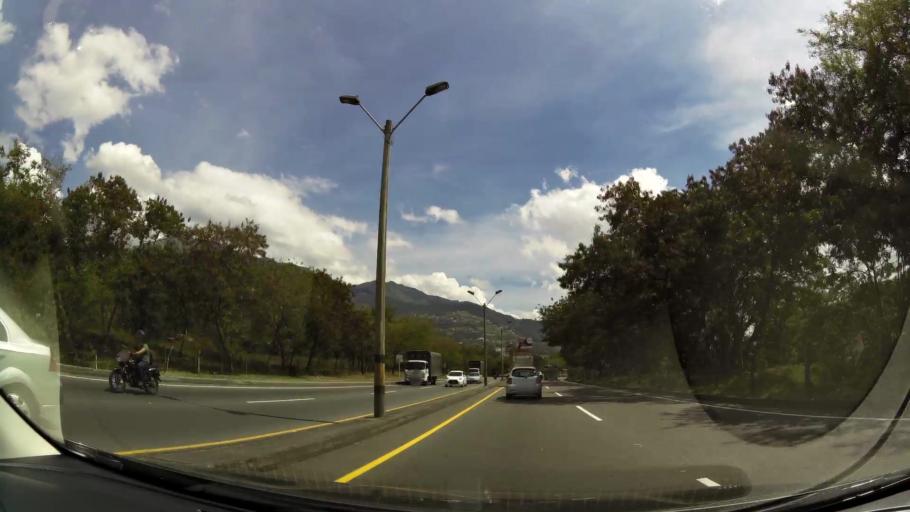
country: CO
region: Antioquia
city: Bello
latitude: 6.3312
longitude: -75.5496
